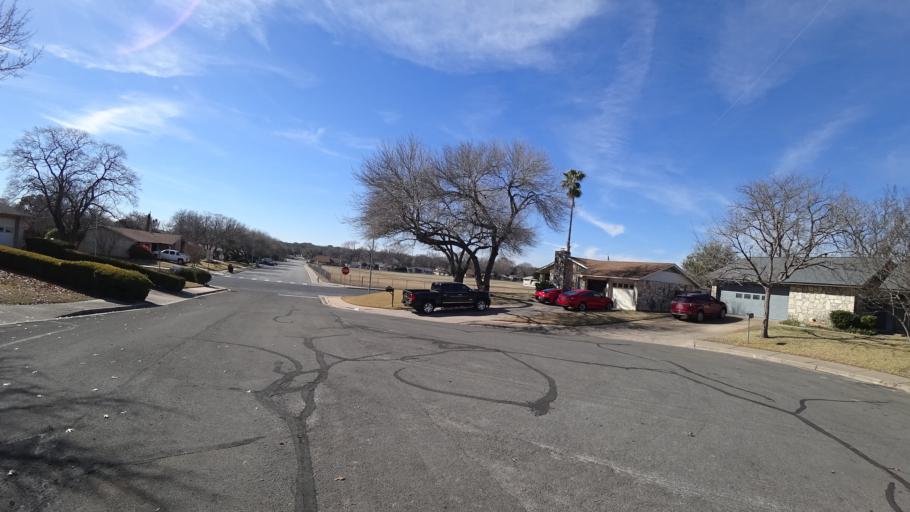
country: US
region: Texas
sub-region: Travis County
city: Wells Branch
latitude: 30.3769
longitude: -97.7029
